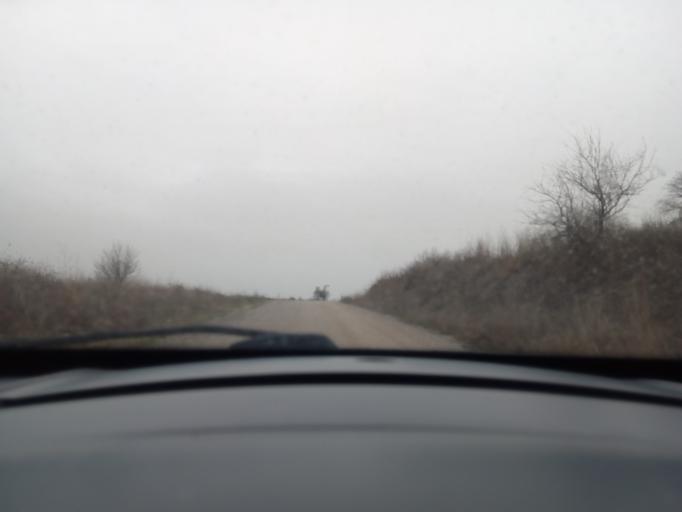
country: TR
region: Balikesir
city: Susurluk
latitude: 39.9107
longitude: 28.1180
